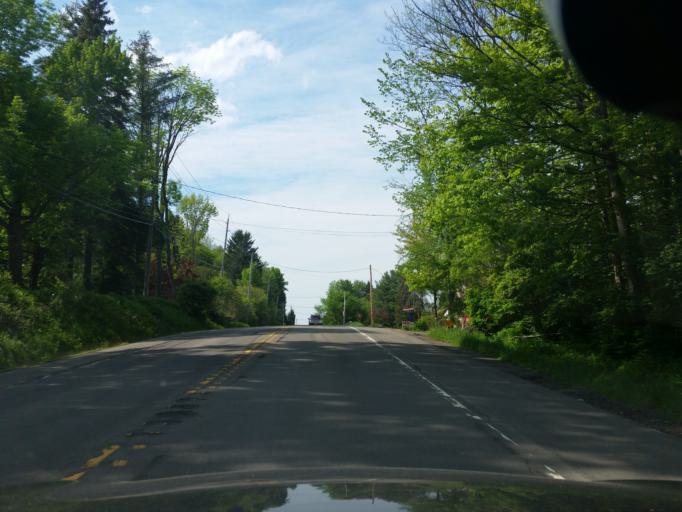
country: US
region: New York
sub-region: Chautauqua County
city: Lakewood
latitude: 42.1222
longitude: -79.3912
